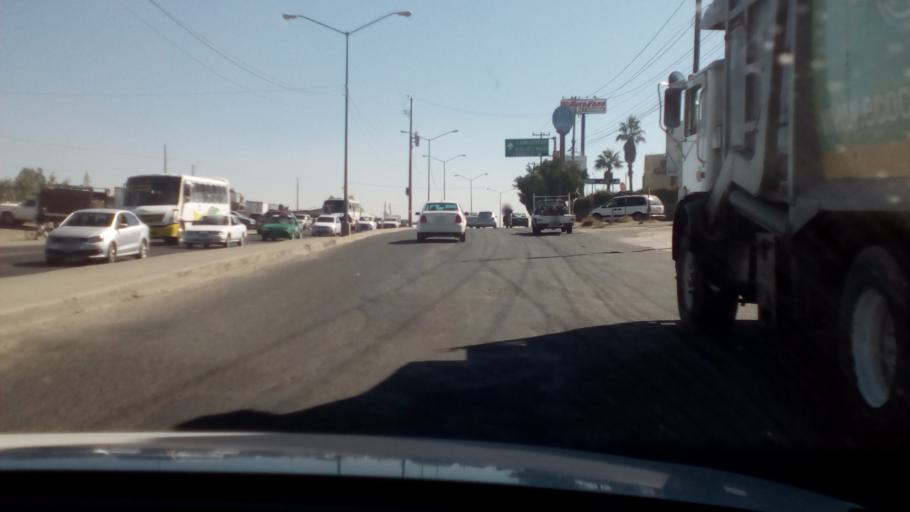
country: MX
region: Guanajuato
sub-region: Leon
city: Ejido la Joya
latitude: 21.1353
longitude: -101.7213
